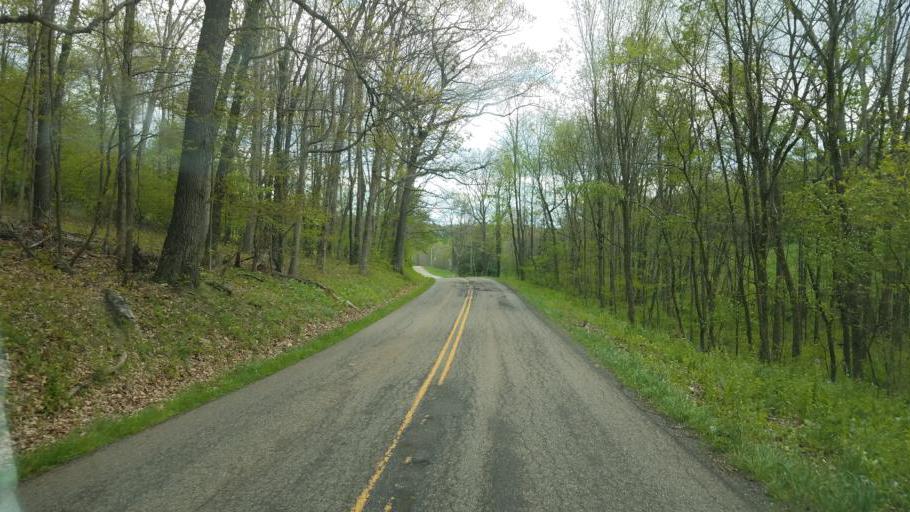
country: US
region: Ohio
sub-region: Knox County
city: Danville
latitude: 40.5394
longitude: -82.2853
